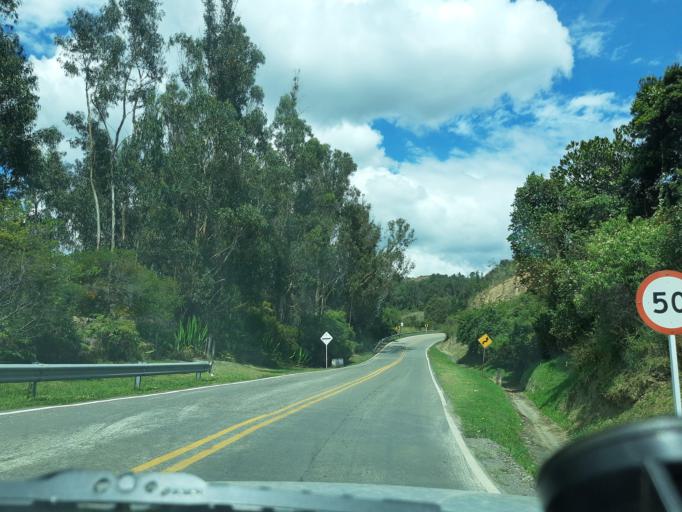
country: CO
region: Boyaca
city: Raquira
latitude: 5.5681
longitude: -73.6818
